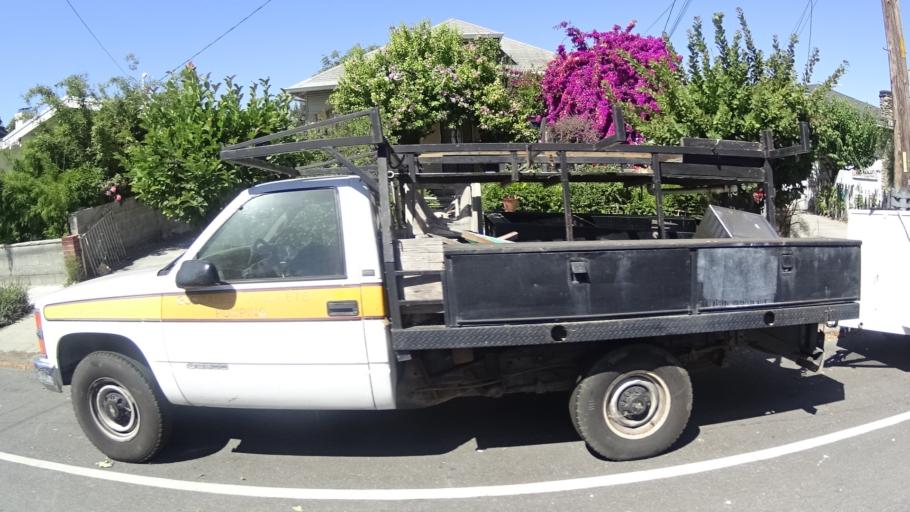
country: US
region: California
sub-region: Santa Clara County
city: San Jose
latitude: 37.3501
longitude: -121.8841
